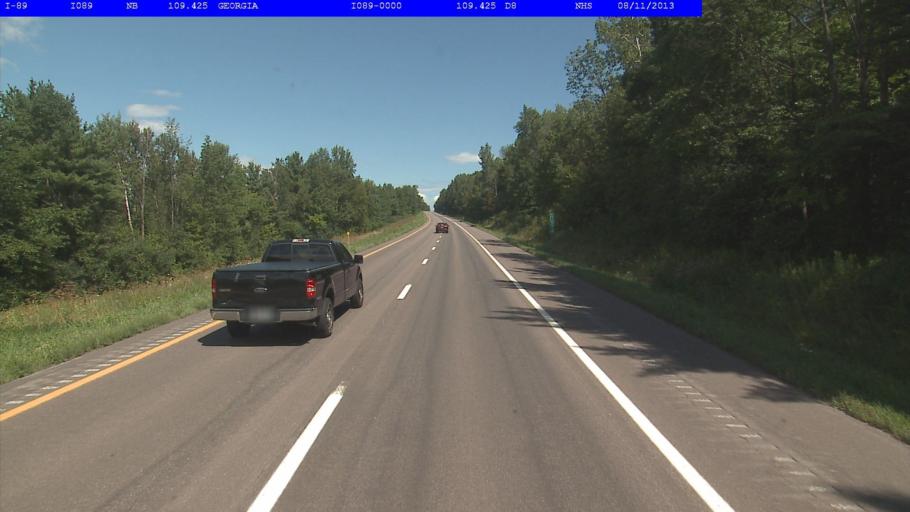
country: US
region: Vermont
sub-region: Franklin County
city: Saint Albans
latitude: 44.7327
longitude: -73.0796
